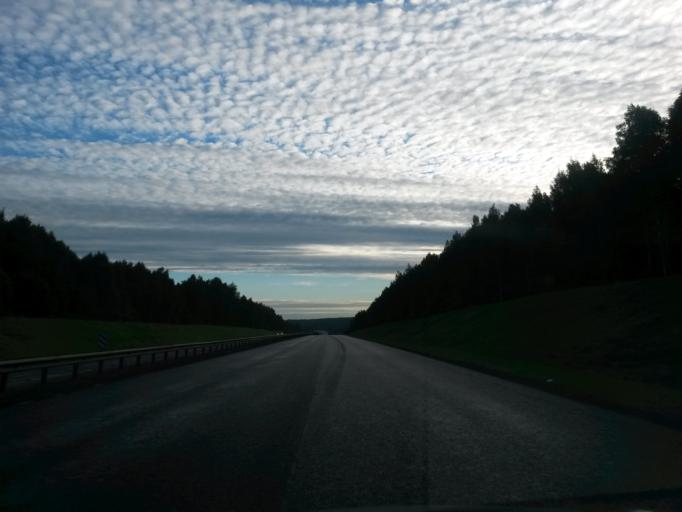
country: RU
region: Vladimir
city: Strunino
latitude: 56.5241
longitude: 38.5659
